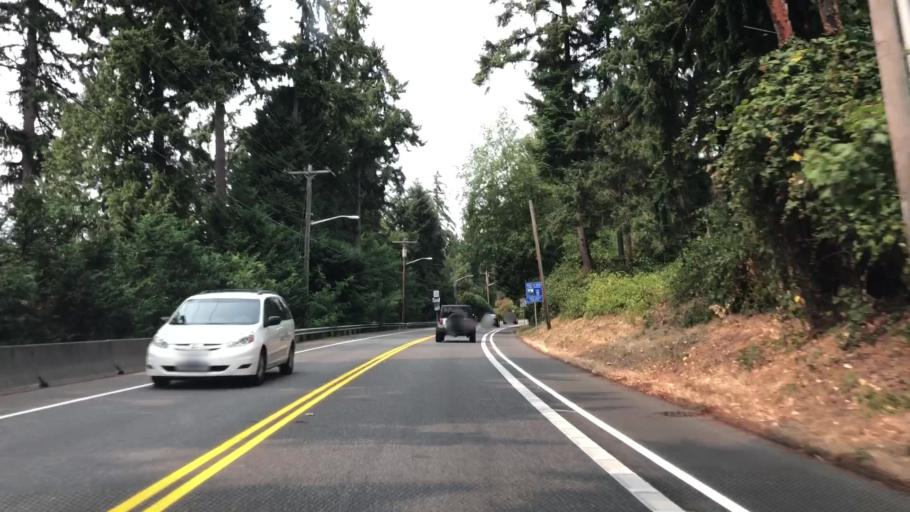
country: US
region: Washington
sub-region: King County
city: Inglewood-Finn Hill
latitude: 47.7013
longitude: -122.2355
